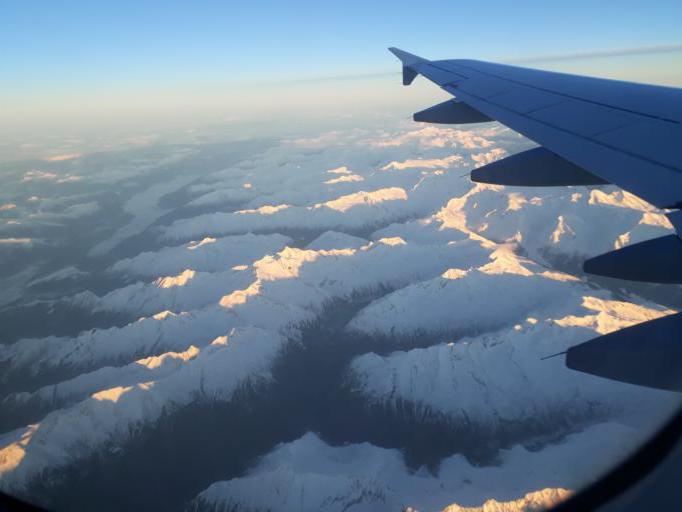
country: AT
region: Tyrol
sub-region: Politischer Bezirk Schwaz
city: Mayrhofen
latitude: 47.1003
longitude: 11.8740
